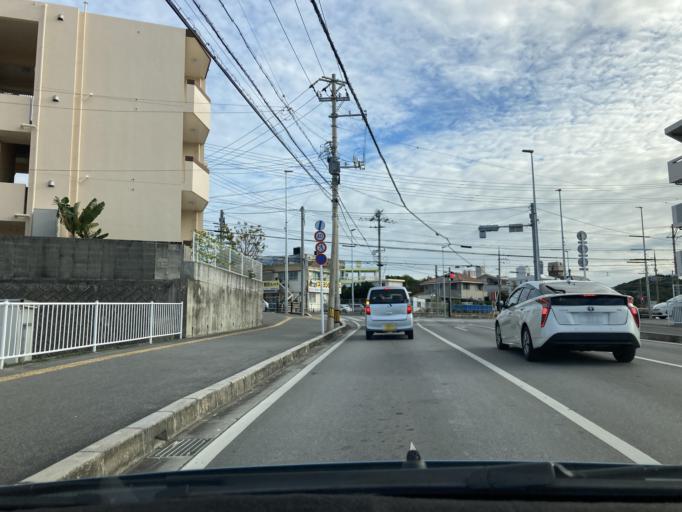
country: JP
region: Okinawa
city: Tomigusuku
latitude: 26.1984
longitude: 127.7328
